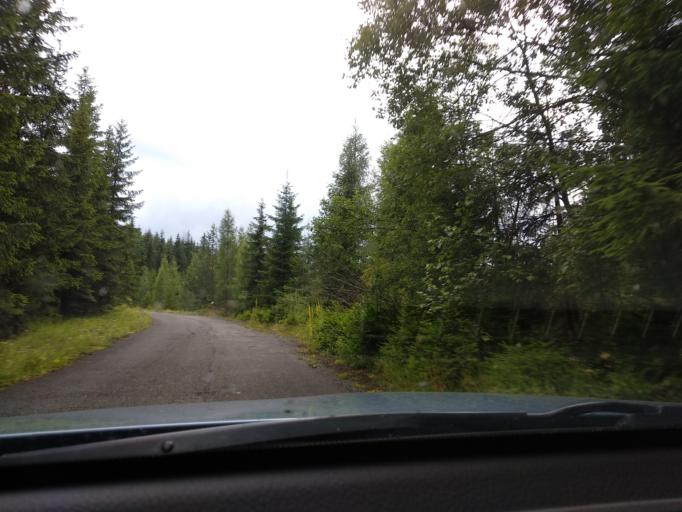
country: SK
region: Zilinsky
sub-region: Okres Liptovsky Mikulas
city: Hybe
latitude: 49.0197
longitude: 19.9013
